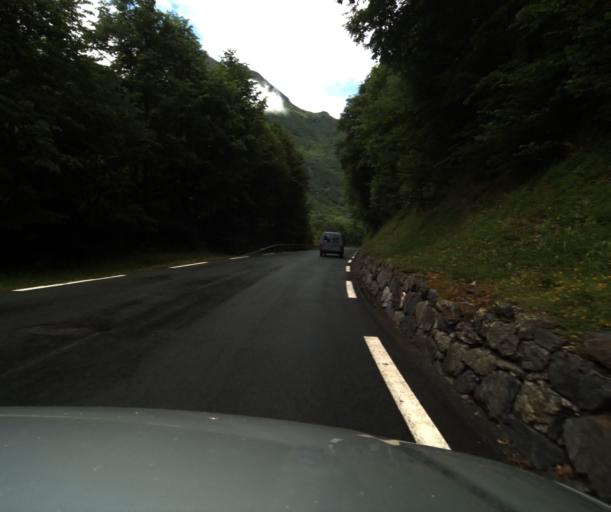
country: FR
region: Midi-Pyrenees
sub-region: Departement des Hautes-Pyrenees
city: Luz-Saint-Sauveur
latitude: 42.8059
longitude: 0.0119
